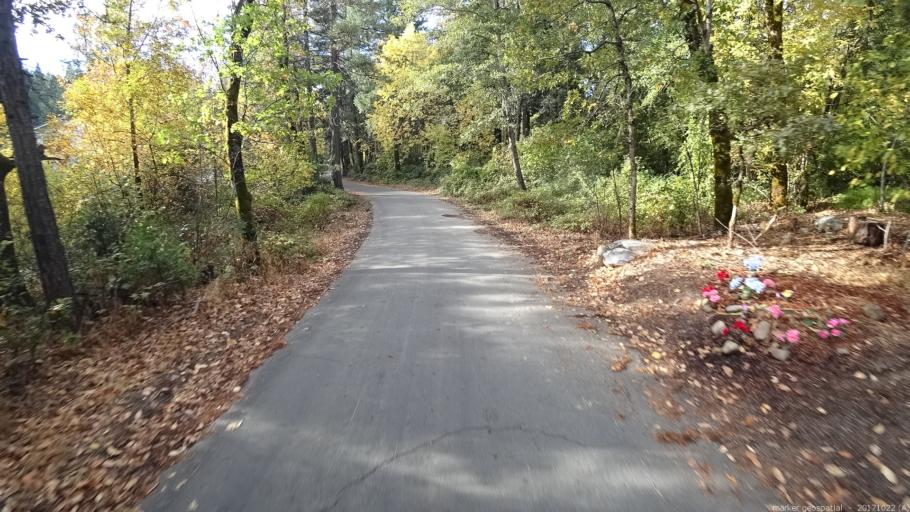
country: US
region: California
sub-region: Siskiyou County
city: Dunsmuir
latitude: 41.1432
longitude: -122.3146
